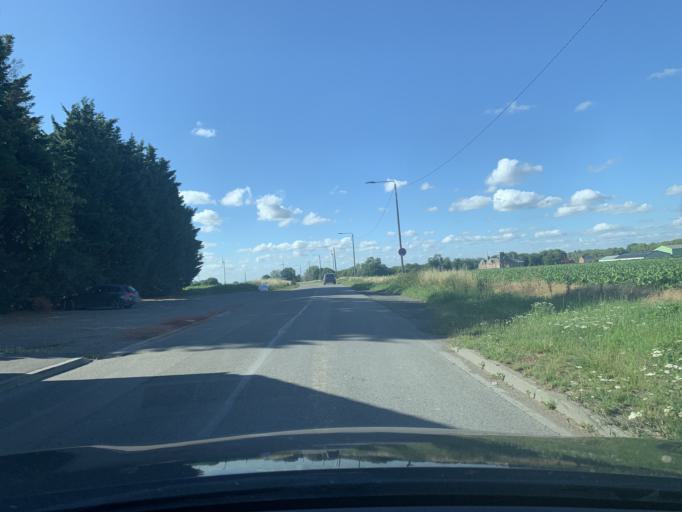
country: FR
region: Nord-Pas-de-Calais
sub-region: Departement du Nord
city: Lauwin-Planque
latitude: 50.3731
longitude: 3.0262
